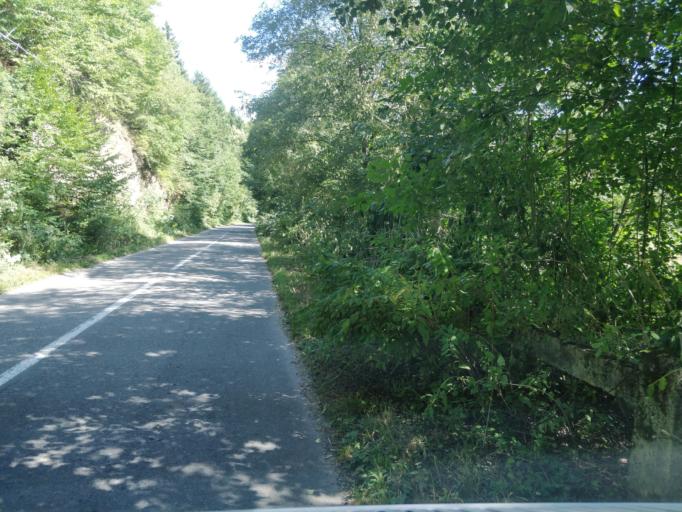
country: RO
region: Cluj
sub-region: Comuna Sacueu
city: Sacuieu
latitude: 46.8520
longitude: 22.8616
